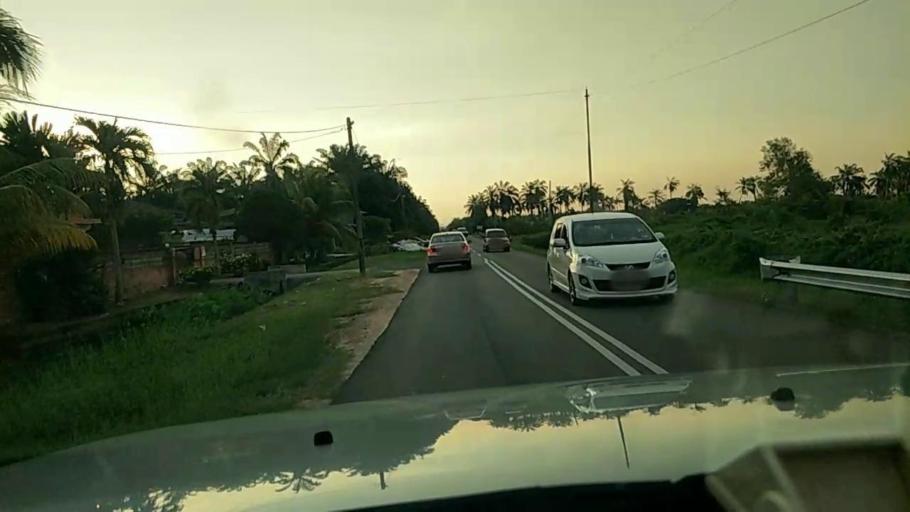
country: MY
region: Selangor
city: Kuala Selangor
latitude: 3.3162
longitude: 101.2815
